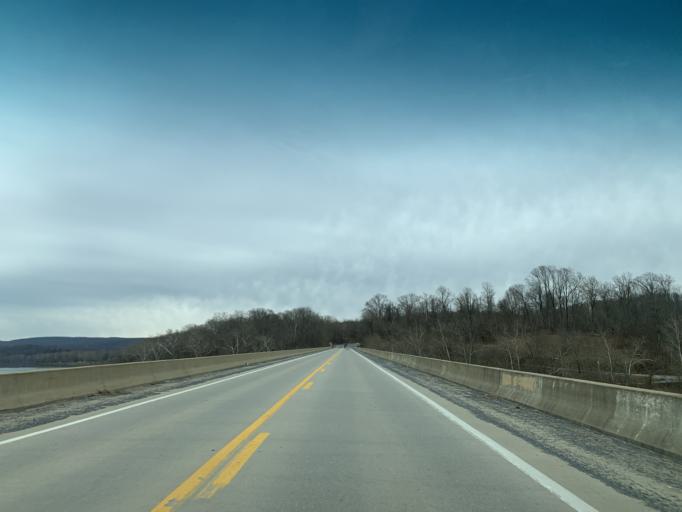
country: US
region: West Virginia
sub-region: Jefferson County
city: Shannondale
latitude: 39.2546
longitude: -77.8173
